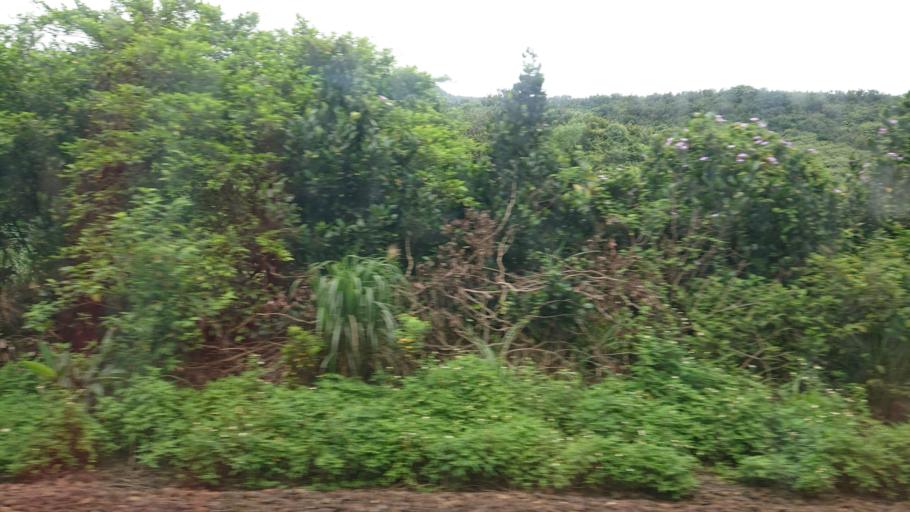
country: TW
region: Taiwan
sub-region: Keelung
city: Keelung
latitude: 25.0092
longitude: 121.9547
